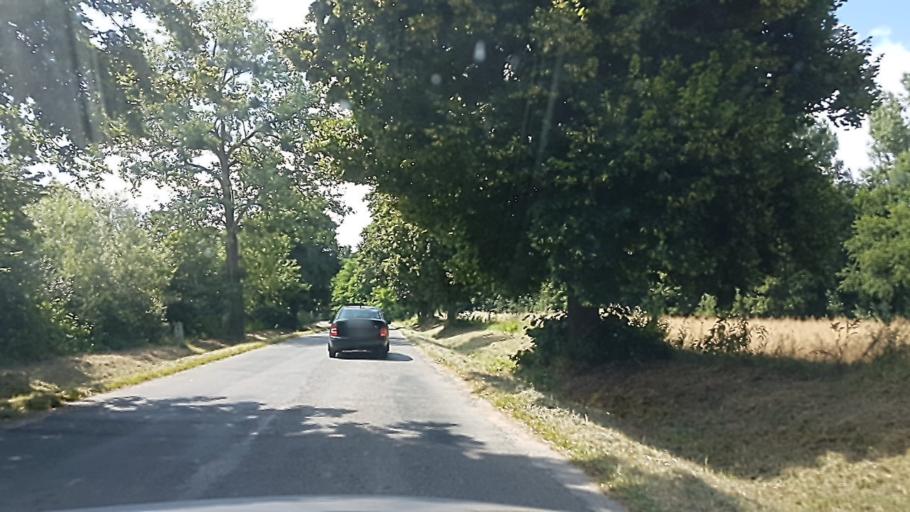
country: HU
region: Somogy
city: Barcs
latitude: 45.9603
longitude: 17.5952
